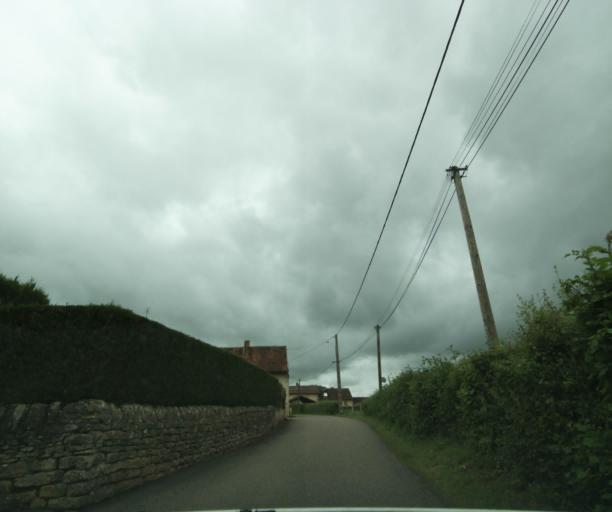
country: FR
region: Bourgogne
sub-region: Departement de Saone-et-Loire
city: Charolles
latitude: 46.4404
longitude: 4.2764
